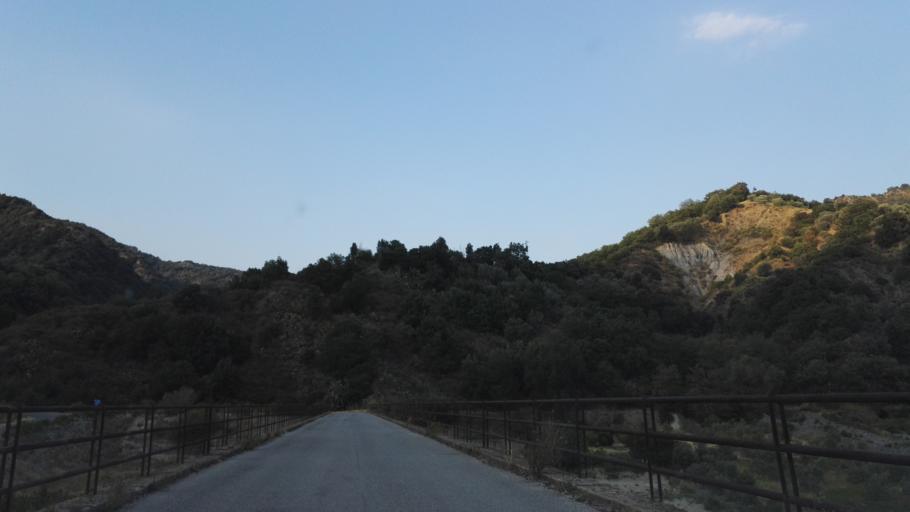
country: IT
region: Calabria
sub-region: Provincia di Reggio Calabria
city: Caulonia
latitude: 38.4187
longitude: 16.3780
